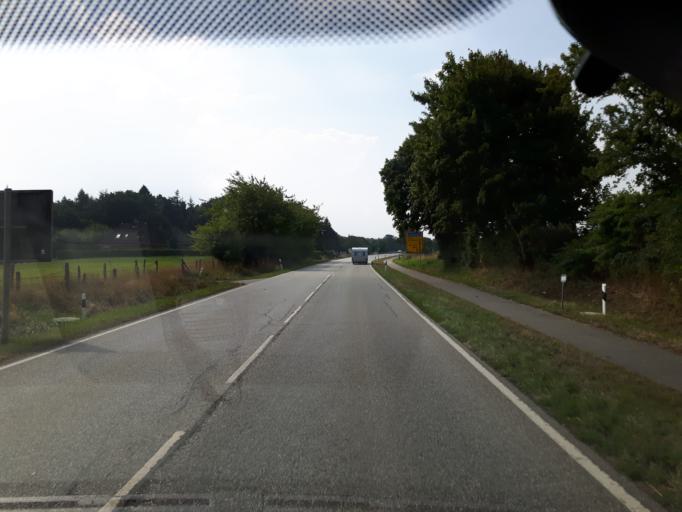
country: DE
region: Schleswig-Holstein
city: Goosefeld
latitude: 54.4388
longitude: 9.8177
